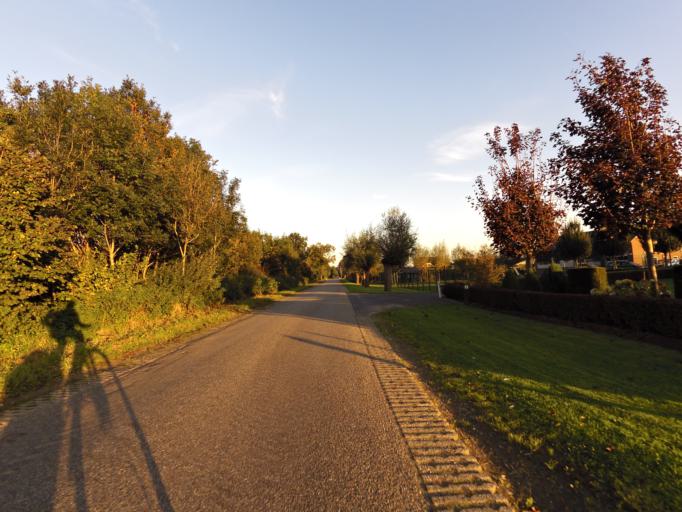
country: NL
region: Gelderland
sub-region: Gemeente Zevenaar
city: Zevenaar
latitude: 51.9223
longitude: 6.1605
